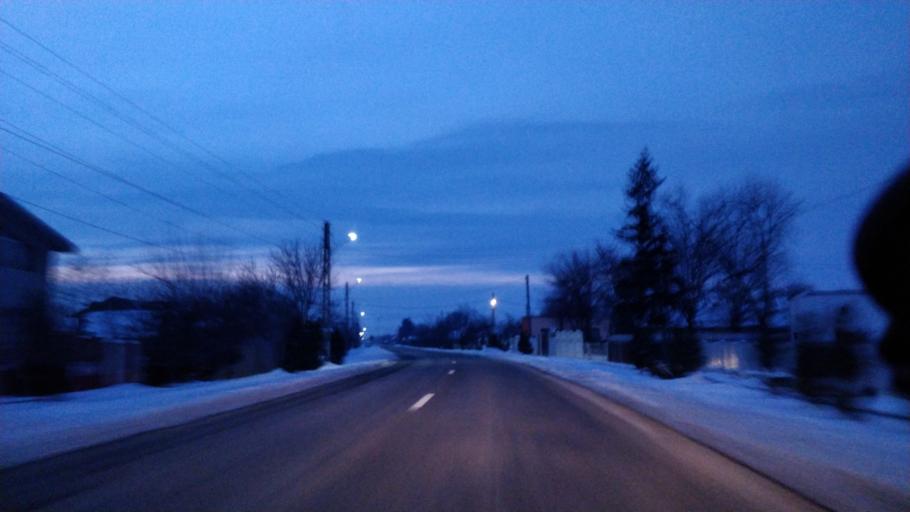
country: RO
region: Vrancea
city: Vulturu de Sus
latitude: 45.6135
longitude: 27.4353
